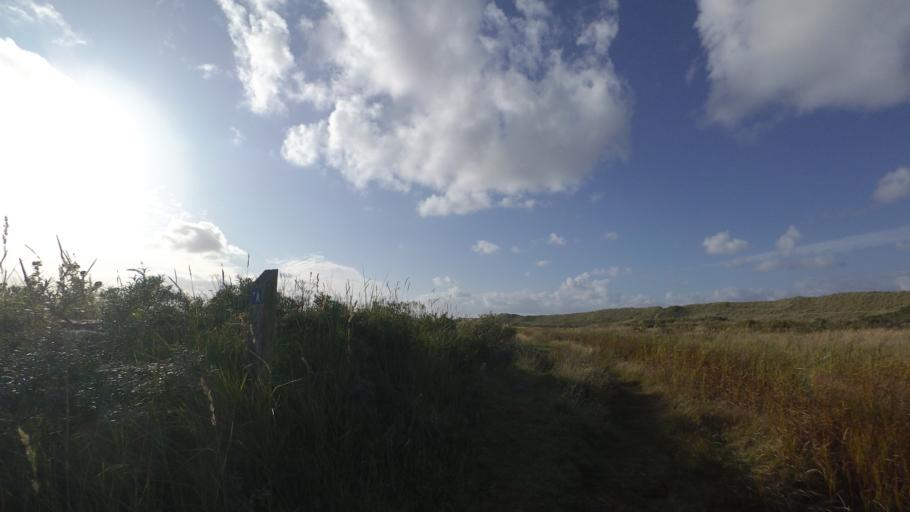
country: NL
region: Friesland
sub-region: Gemeente Dongeradeel
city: Holwerd
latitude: 53.4645
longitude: 5.9137
